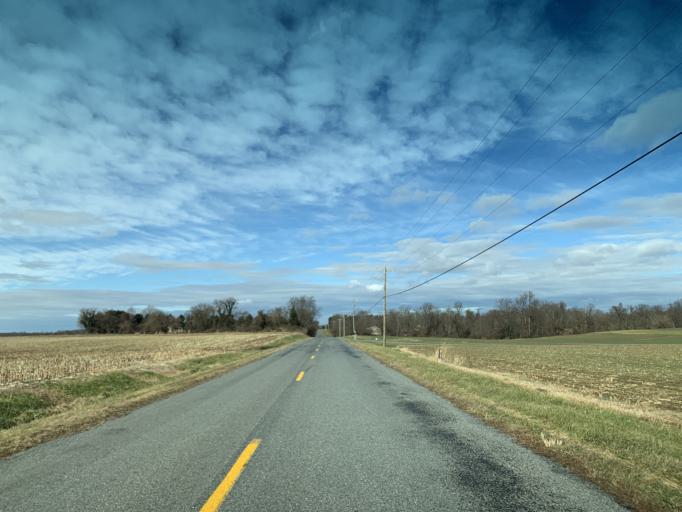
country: US
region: Maryland
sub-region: Kent County
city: Chestertown
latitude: 39.3342
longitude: -76.0458
